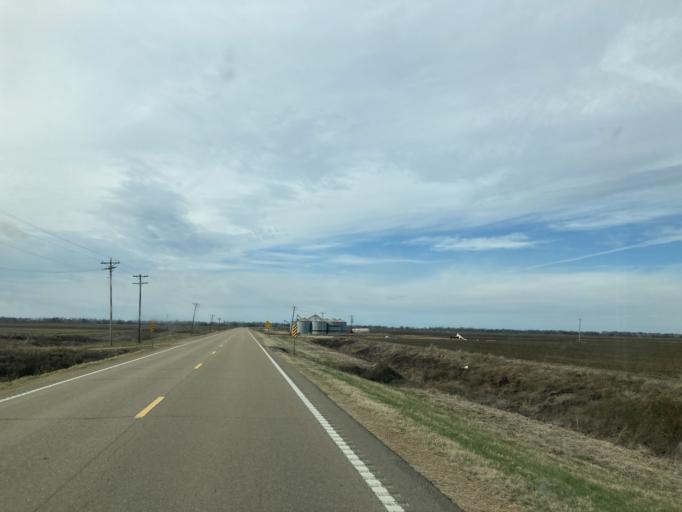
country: US
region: Mississippi
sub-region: Humphreys County
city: Belzoni
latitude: 33.1828
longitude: -90.6466
